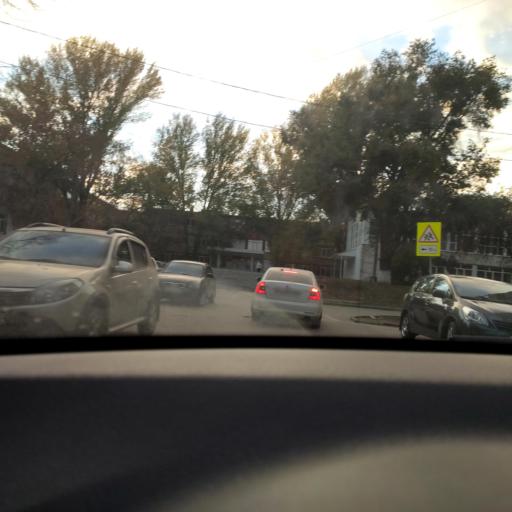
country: RU
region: Samara
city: Samara
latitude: 53.1960
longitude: 50.2044
